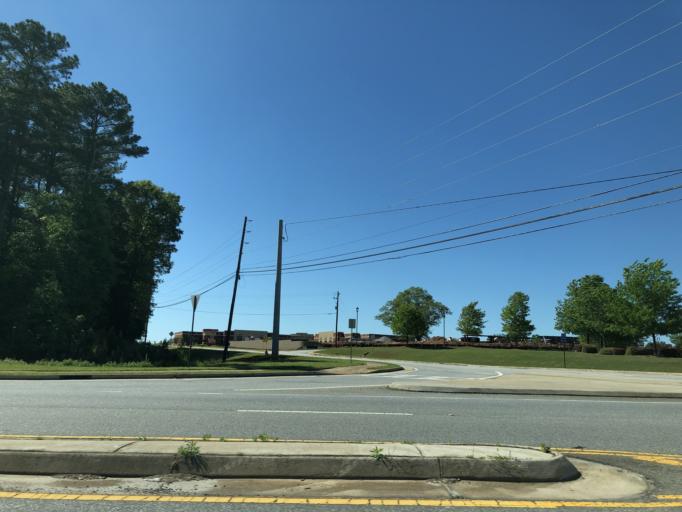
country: US
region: Georgia
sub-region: Oconee County
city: Watkinsville
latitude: 33.9141
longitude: -83.4631
